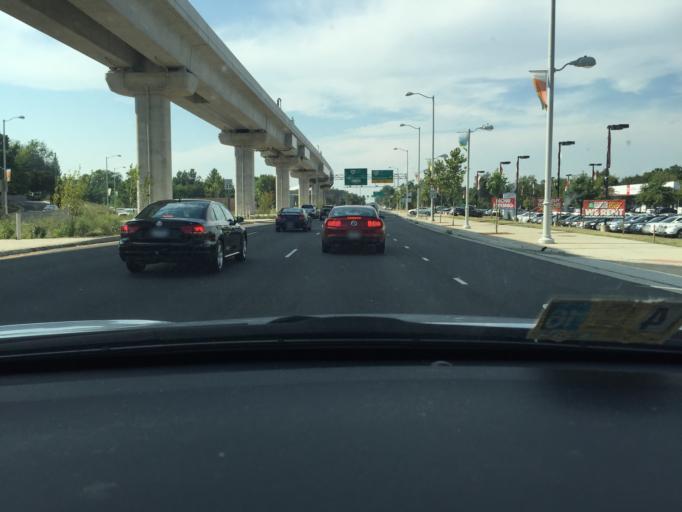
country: US
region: Virginia
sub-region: Fairfax County
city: Tysons Corner
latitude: 38.9310
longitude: -77.2433
